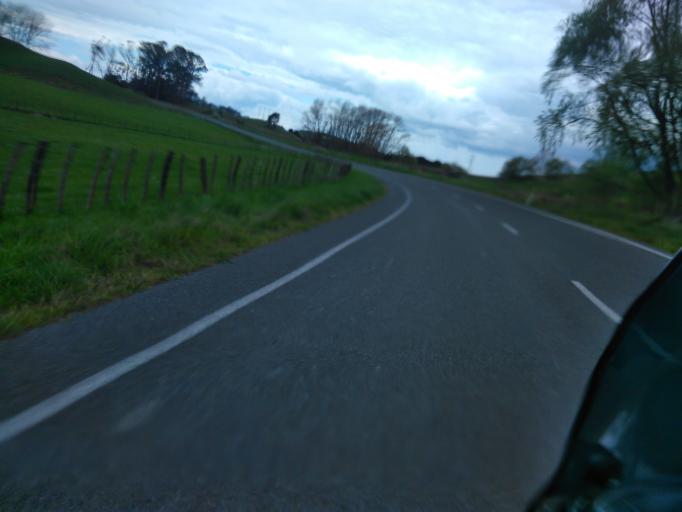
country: NZ
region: Gisborne
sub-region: Gisborne District
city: Gisborne
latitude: -38.6823
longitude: 177.7986
